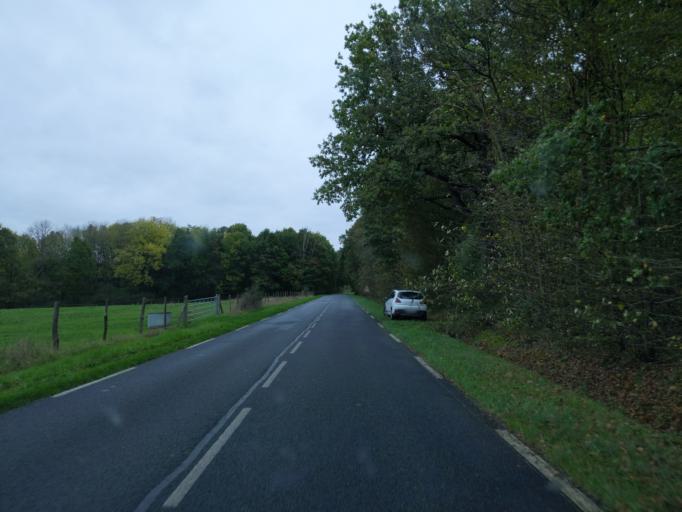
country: FR
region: Ile-de-France
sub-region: Departement des Yvelines
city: Bullion
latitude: 48.6374
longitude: 1.9924
